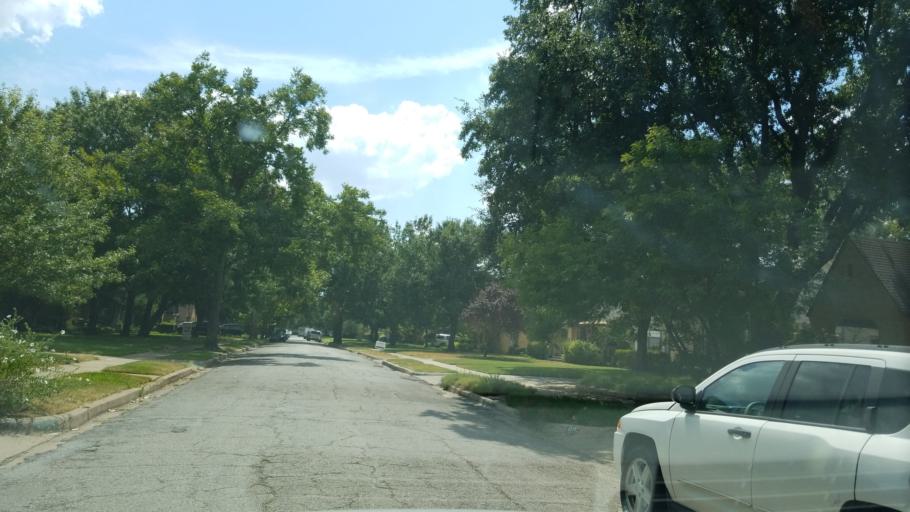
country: US
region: Texas
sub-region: Dallas County
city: Dallas
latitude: 32.7589
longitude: -96.8439
